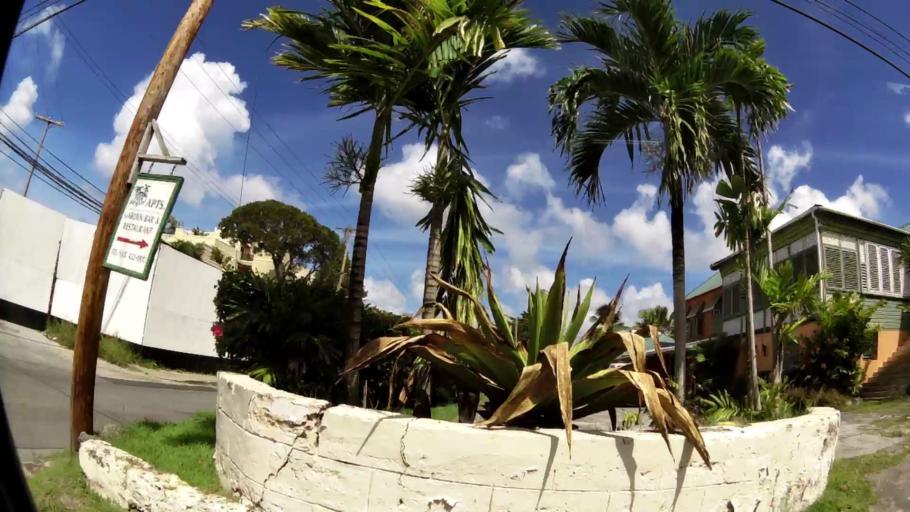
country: BB
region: Saint James
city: Holetown
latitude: 13.1562
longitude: -59.6365
